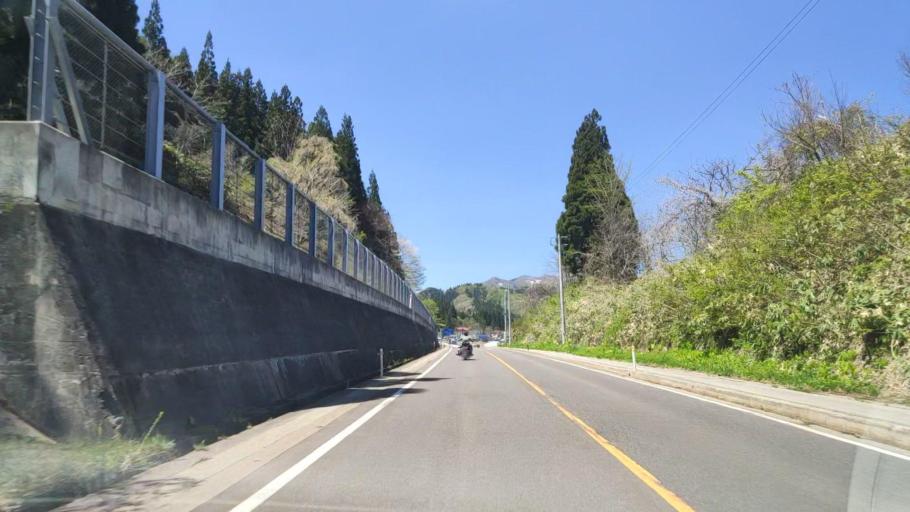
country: JP
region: Akita
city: Yuzawa
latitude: 39.0500
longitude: 140.4113
